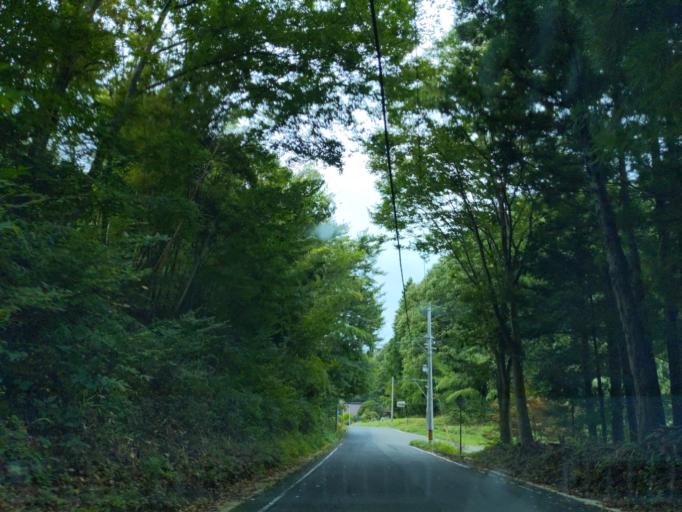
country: JP
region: Fukushima
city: Miharu
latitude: 37.3728
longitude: 140.5291
